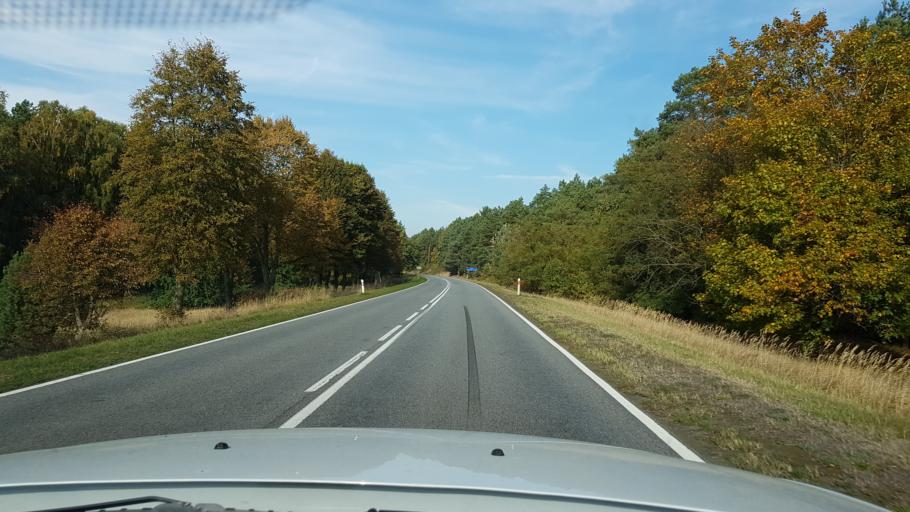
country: PL
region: West Pomeranian Voivodeship
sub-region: Powiat mysliborski
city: Nowogrodek Pomorski
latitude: 52.9166
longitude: 14.9678
